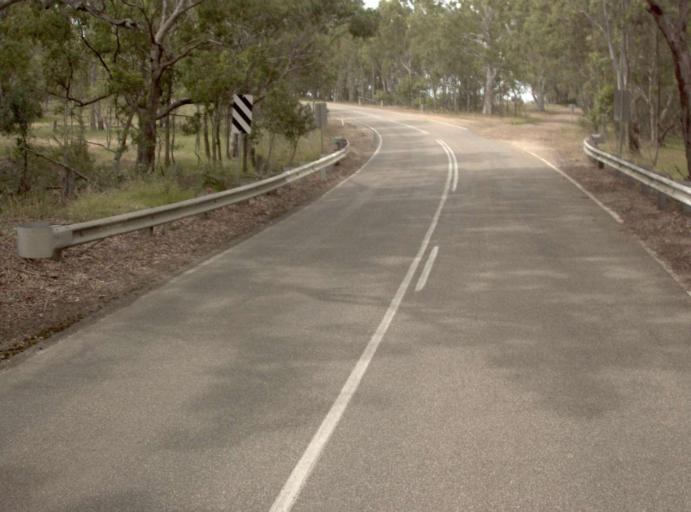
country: AU
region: Victoria
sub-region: Wellington
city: Sale
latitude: -37.8852
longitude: 147.0644
